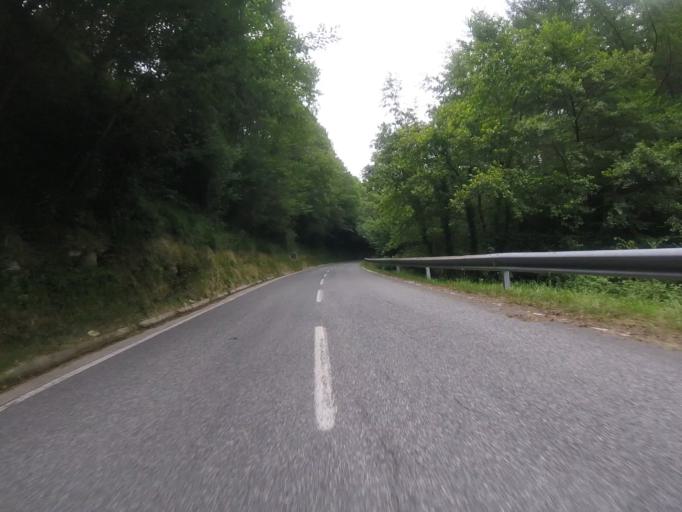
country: ES
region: Navarre
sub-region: Provincia de Navarra
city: Ezkurra
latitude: 43.0865
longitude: -1.8458
